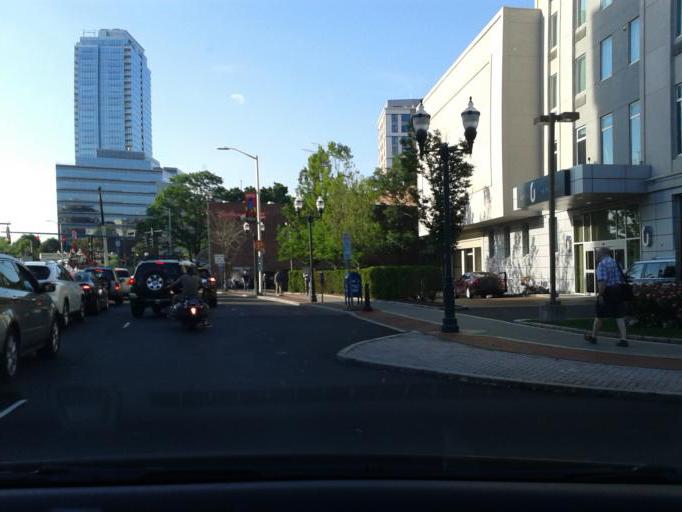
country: US
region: Connecticut
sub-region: Fairfield County
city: Stamford
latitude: 41.0517
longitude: -73.5422
